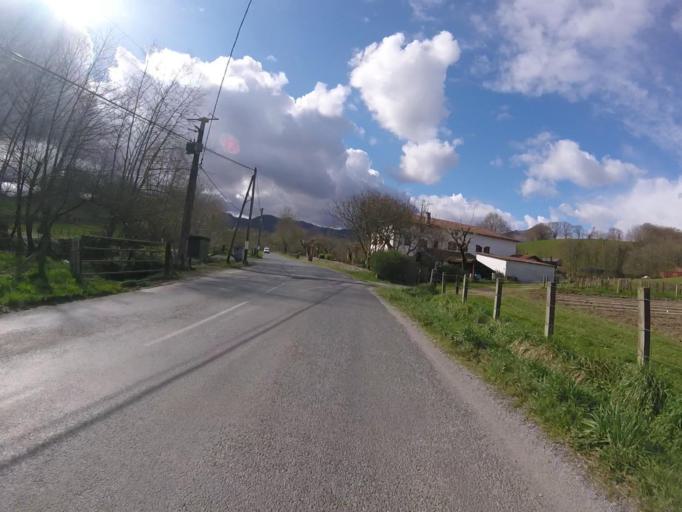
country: FR
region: Aquitaine
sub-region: Departement des Pyrenees-Atlantiques
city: Sare
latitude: 43.2917
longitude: -1.5790
